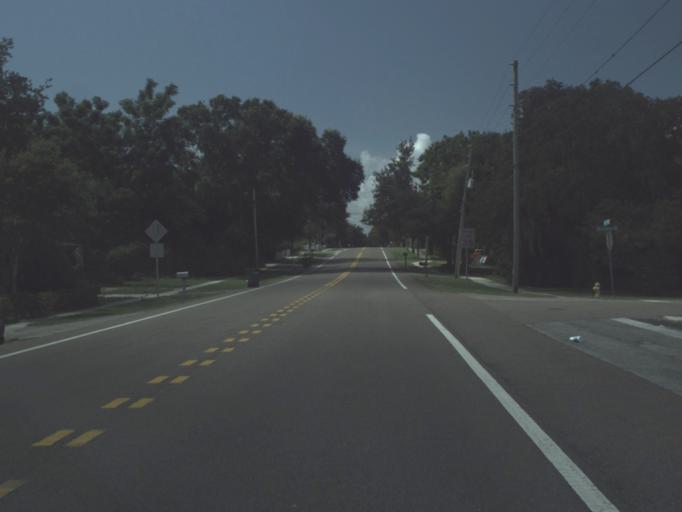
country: US
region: Florida
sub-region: Pinellas County
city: Safety Harbor
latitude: 27.9878
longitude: -82.7023
